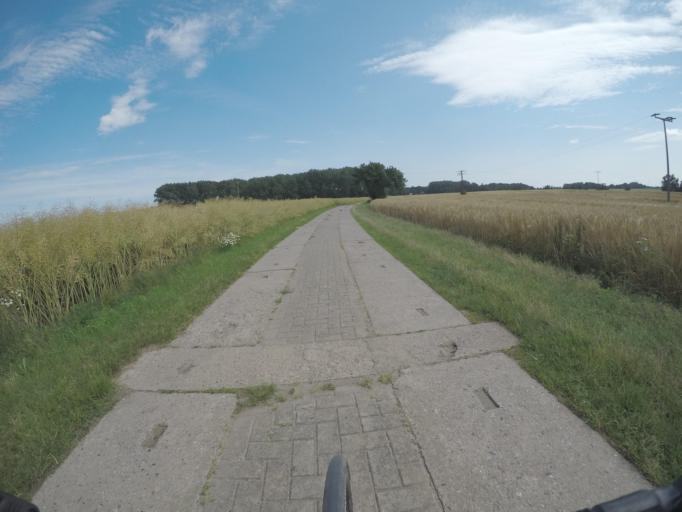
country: DE
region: Mecklenburg-Vorpommern
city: Altefahr
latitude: 54.3685
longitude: 13.1565
